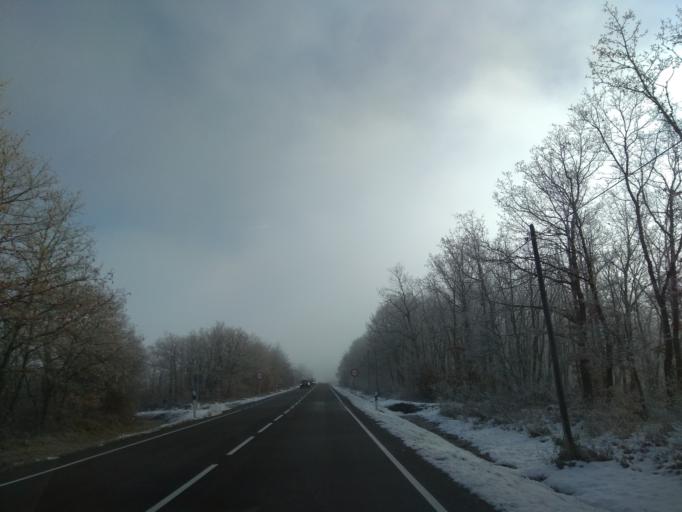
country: ES
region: Castille and Leon
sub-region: Provincia de Burgos
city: Espinosa de los Monteros
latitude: 43.0699
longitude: -3.5188
